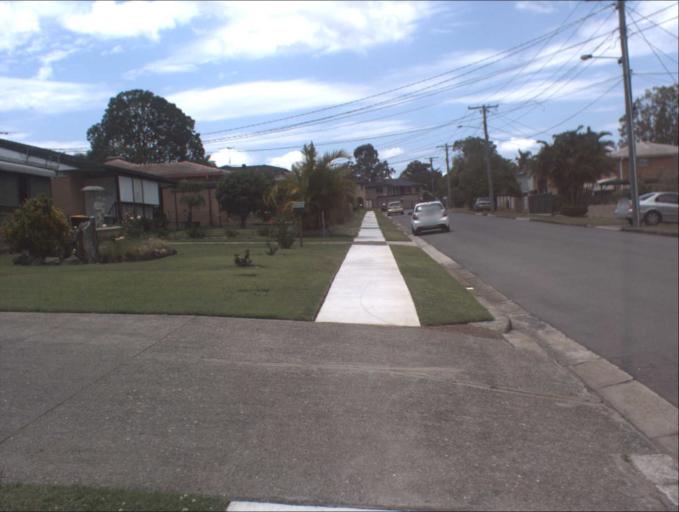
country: AU
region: Queensland
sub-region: Logan
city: Woodridge
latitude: -27.6375
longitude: 153.0993
